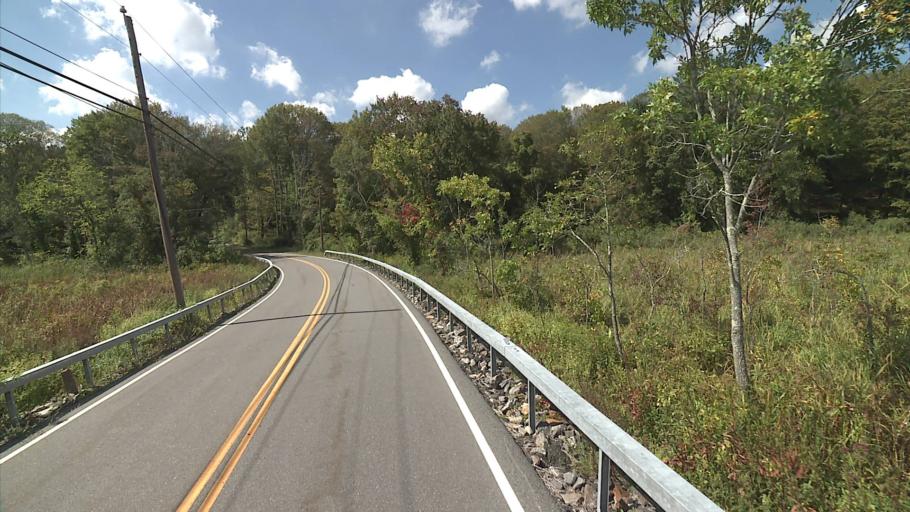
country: US
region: Connecticut
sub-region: Middlesex County
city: Chester Center
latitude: 41.4213
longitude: -72.4211
